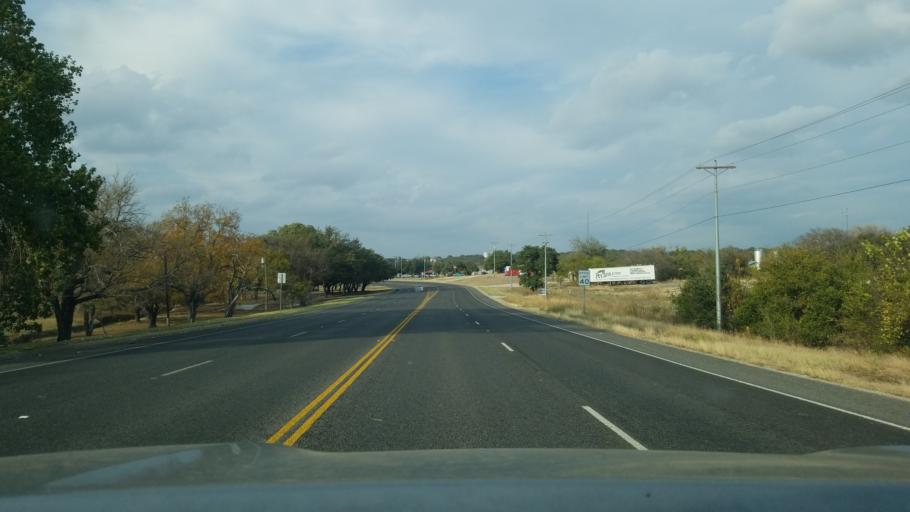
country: US
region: Texas
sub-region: Mills County
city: Goldthwaite
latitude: 31.4432
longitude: -98.5677
